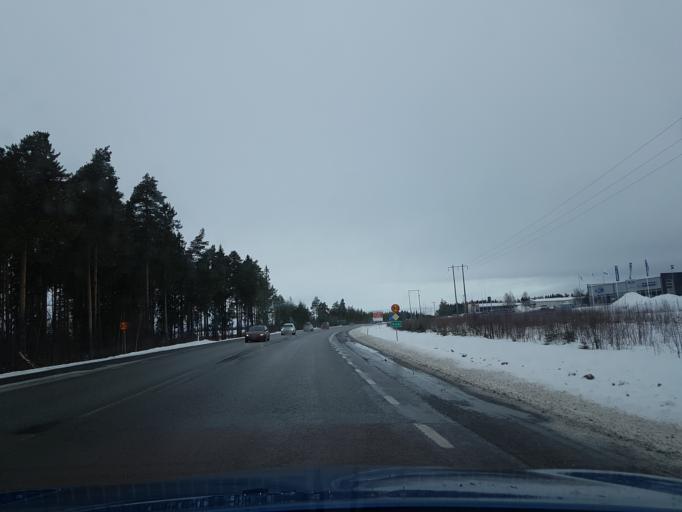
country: SE
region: Dalarna
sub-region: Mora Kommun
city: Mora
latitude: 61.0172
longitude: 14.5887
